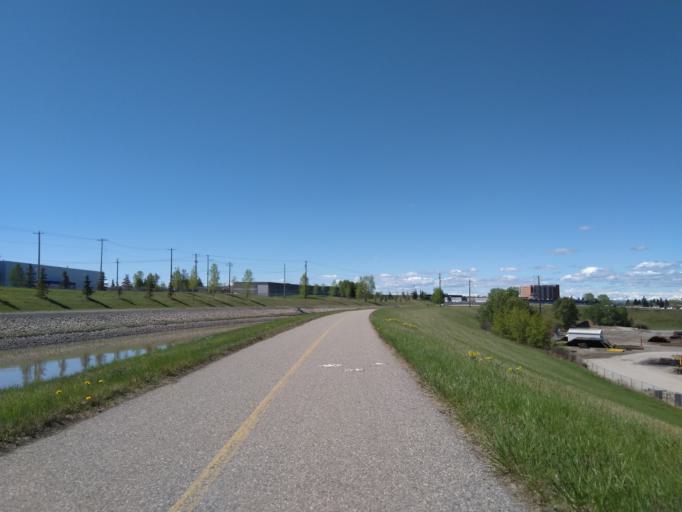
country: CA
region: Alberta
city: Calgary
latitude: 50.9848
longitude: -113.9896
